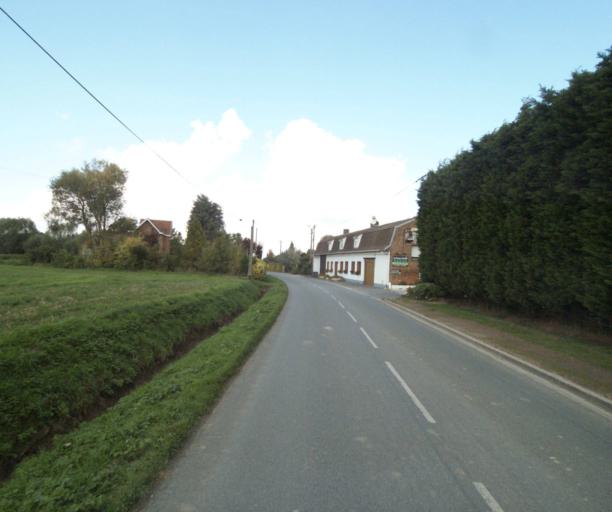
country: FR
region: Nord-Pas-de-Calais
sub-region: Departement du Nord
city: Herlies
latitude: 50.5827
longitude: 2.8444
